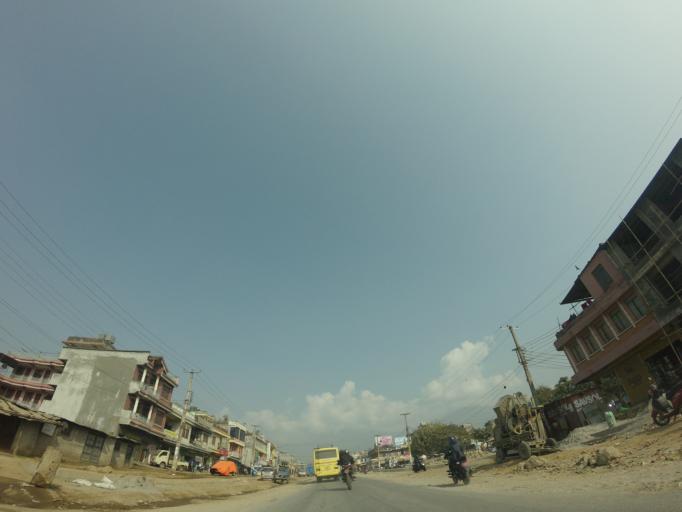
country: NP
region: Western Region
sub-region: Gandaki Zone
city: Pokhara
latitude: 28.2316
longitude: 83.9824
